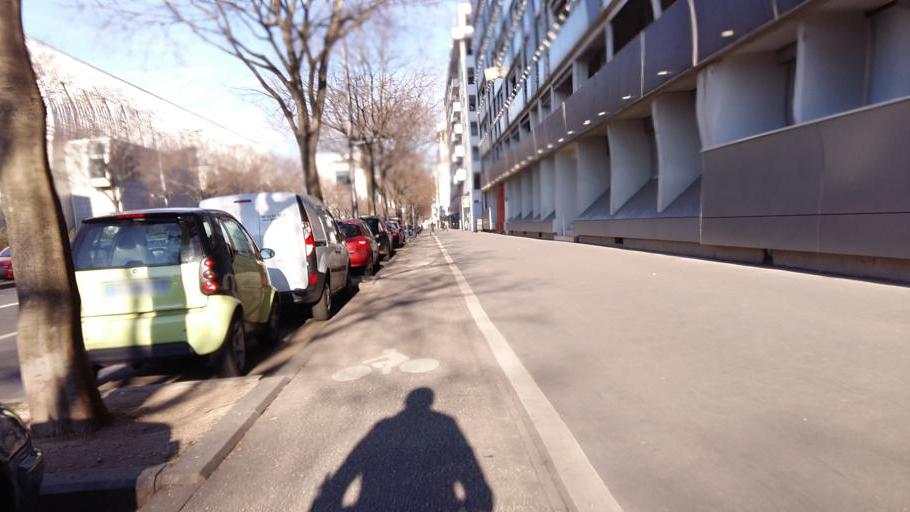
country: FR
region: Rhone-Alpes
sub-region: Departement du Rhone
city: Lyon
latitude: 45.7325
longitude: 4.8344
